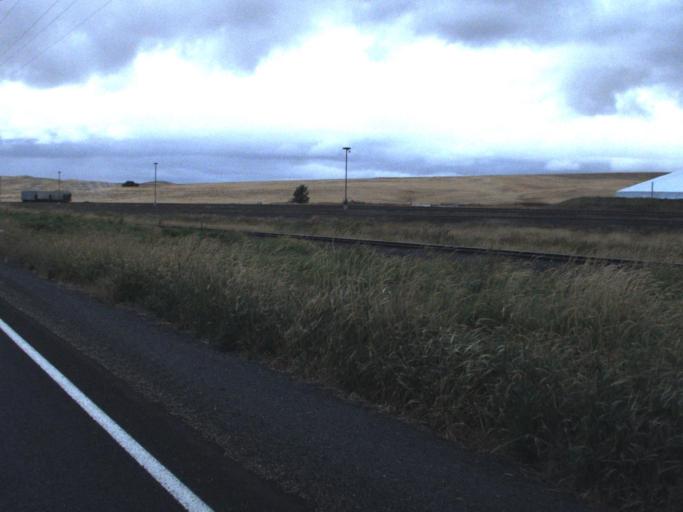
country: US
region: Washington
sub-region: Whitman County
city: Colfax
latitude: 47.1872
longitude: -117.3172
